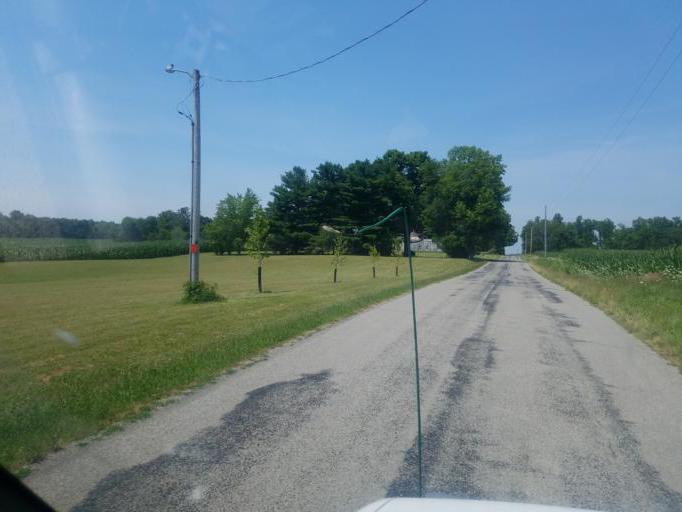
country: US
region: Ohio
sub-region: Logan County
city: West Liberty
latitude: 40.2896
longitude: -83.7864
